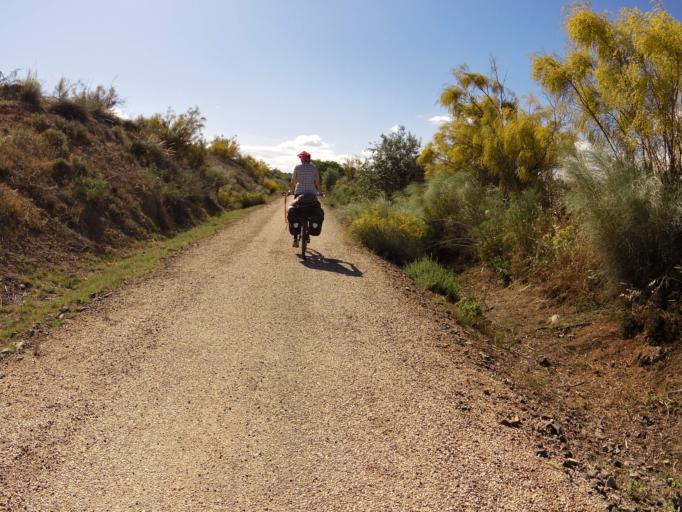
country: ES
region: Andalusia
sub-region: Provincia de Jaen
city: Alcaudete
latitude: 37.6046
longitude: -4.1528
